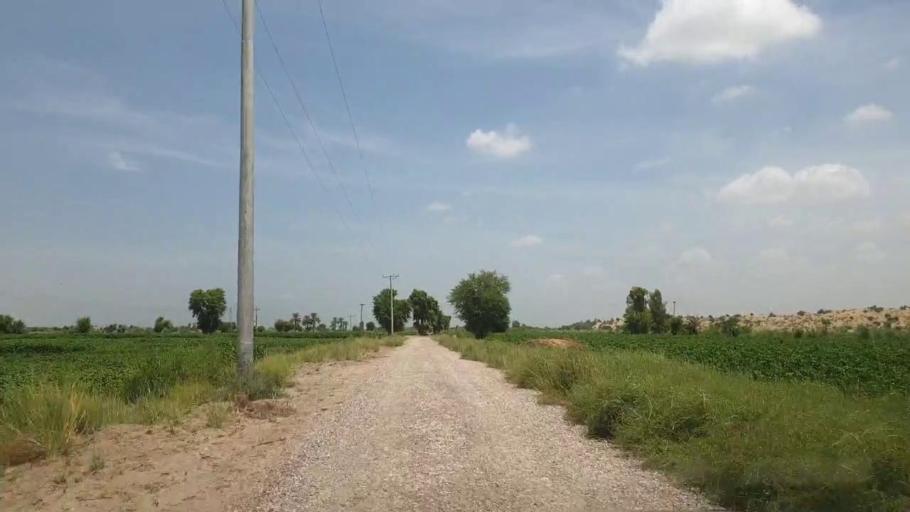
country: PK
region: Sindh
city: Kot Diji
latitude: 27.1505
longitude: 69.0171
